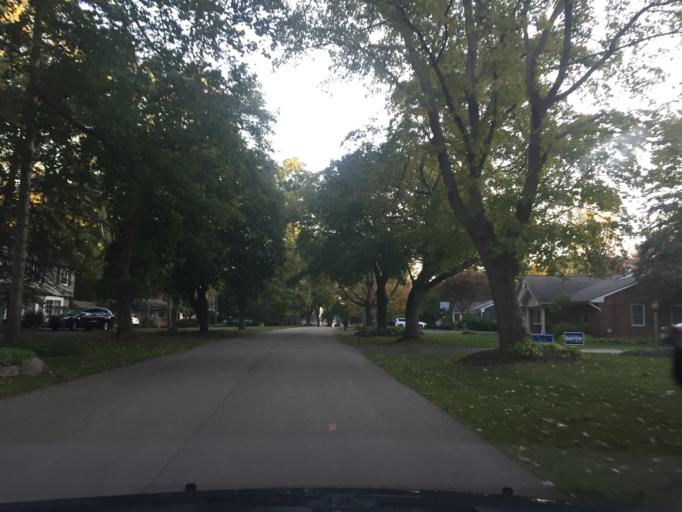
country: US
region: Michigan
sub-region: Oakland County
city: Franklin
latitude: 42.5486
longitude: -83.2924
